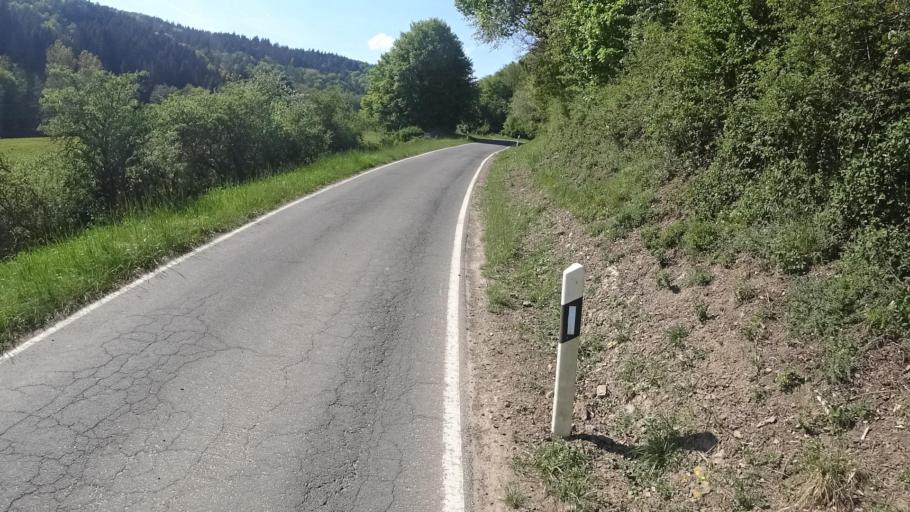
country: DE
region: Rheinland-Pfalz
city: Sierscheid
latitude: 50.4631
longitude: 6.9297
